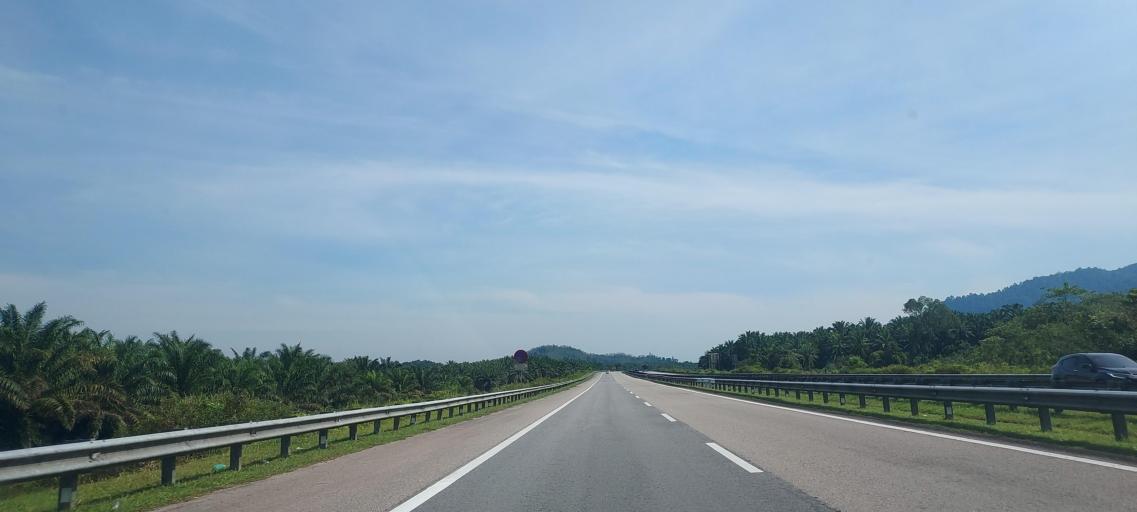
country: MY
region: Terengganu
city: Marang
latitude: 4.9598
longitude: 103.0826
